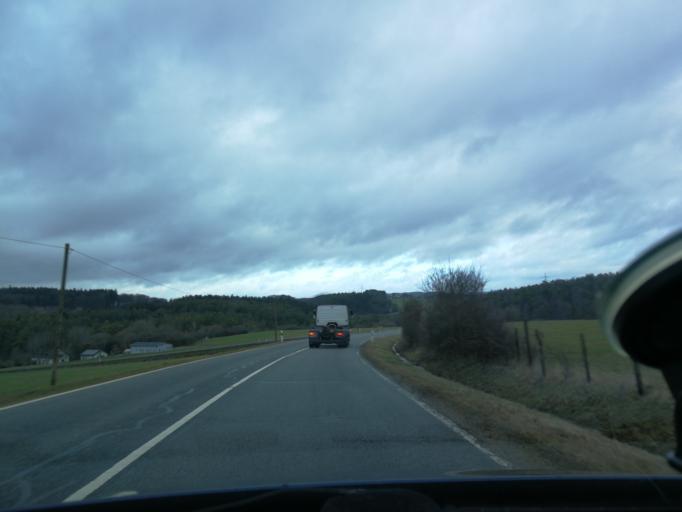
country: DE
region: Rheinland-Pfalz
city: Nohn
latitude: 50.3113
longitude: 6.7724
